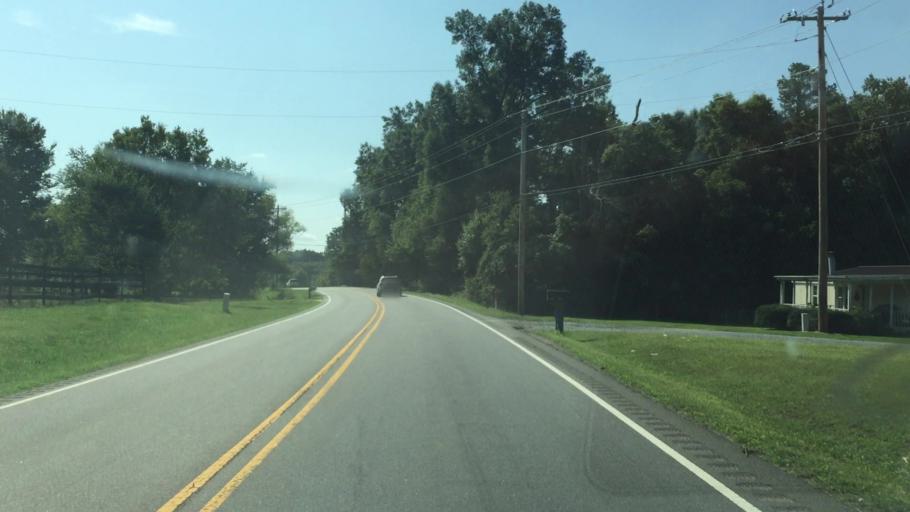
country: US
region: North Carolina
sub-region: Union County
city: Fairview
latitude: 35.1540
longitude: -80.5601
